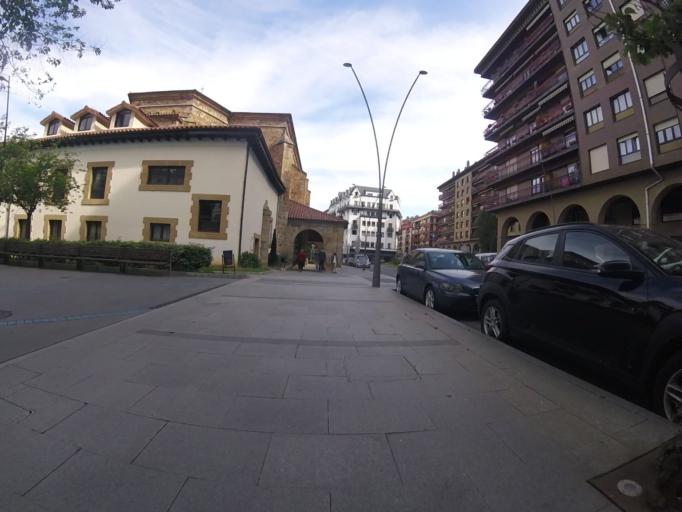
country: ES
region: Basque Country
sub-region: Provincia de Guipuzcoa
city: Zumarraga
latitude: 43.0884
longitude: -2.3131
